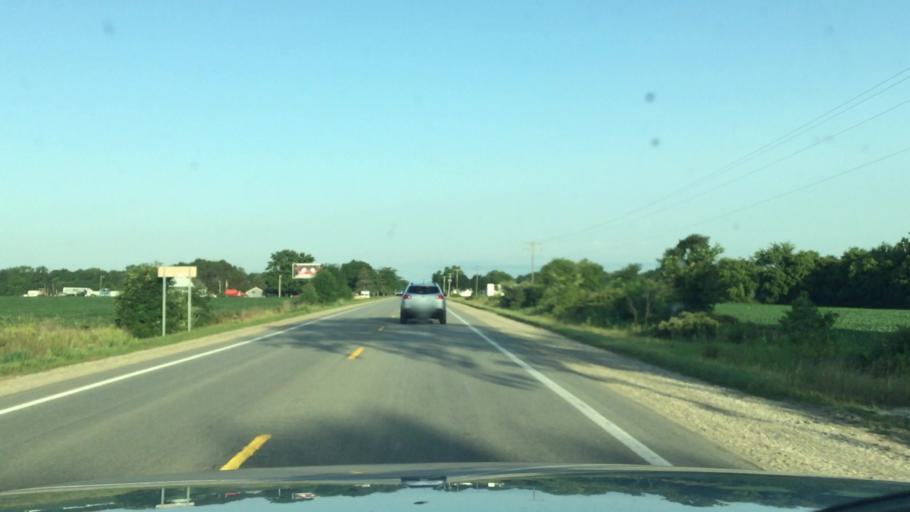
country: US
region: Michigan
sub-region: Gratiot County
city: Ithaca
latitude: 43.1761
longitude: -84.6617
